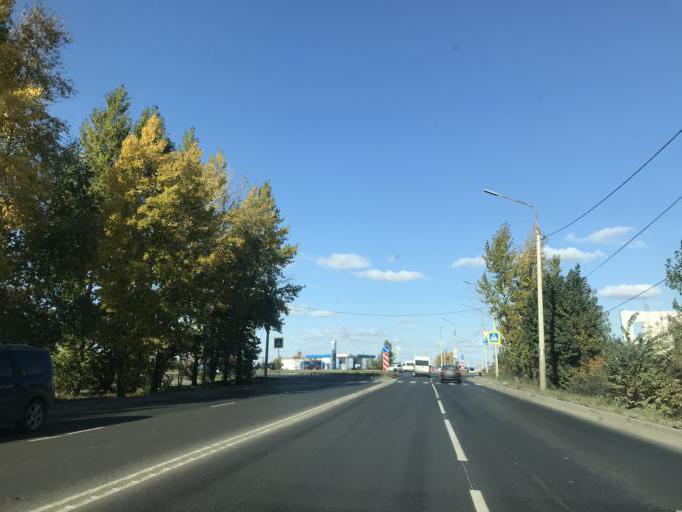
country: RU
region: Chelyabinsk
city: Roshchino
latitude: 55.2394
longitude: 61.3185
